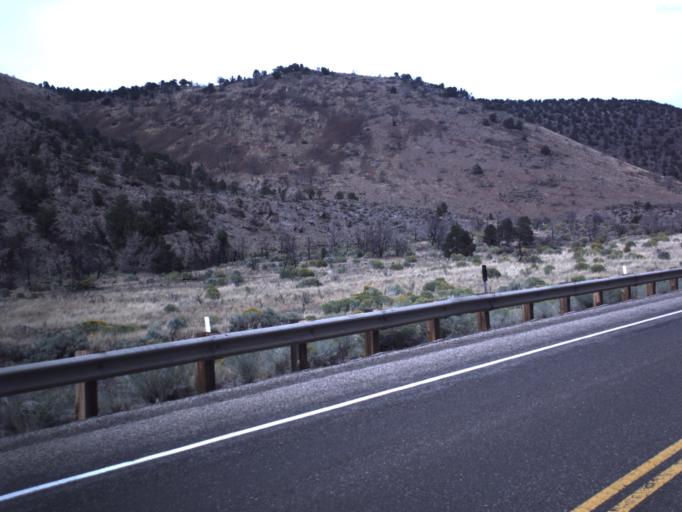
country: US
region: Utah
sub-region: Piute County
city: Junction
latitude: 38.1237
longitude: -112.3318
